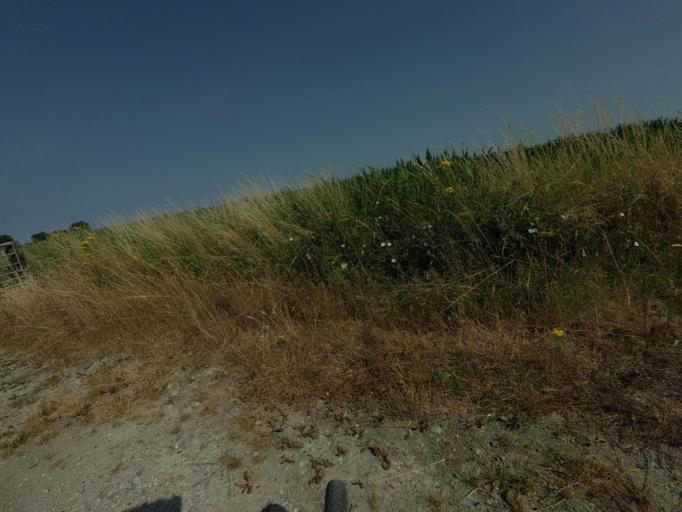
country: BE
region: Flanders
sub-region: Provincie West-Vlaanderen
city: Gistel
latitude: 51.1682
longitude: 2.9750
